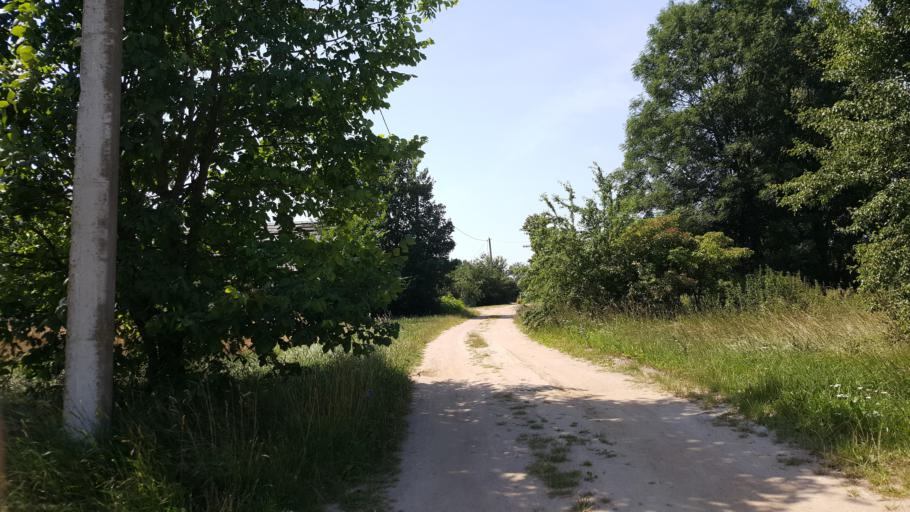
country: BY
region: Brest
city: Vysokaye
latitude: 52.3623
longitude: 23.5337
